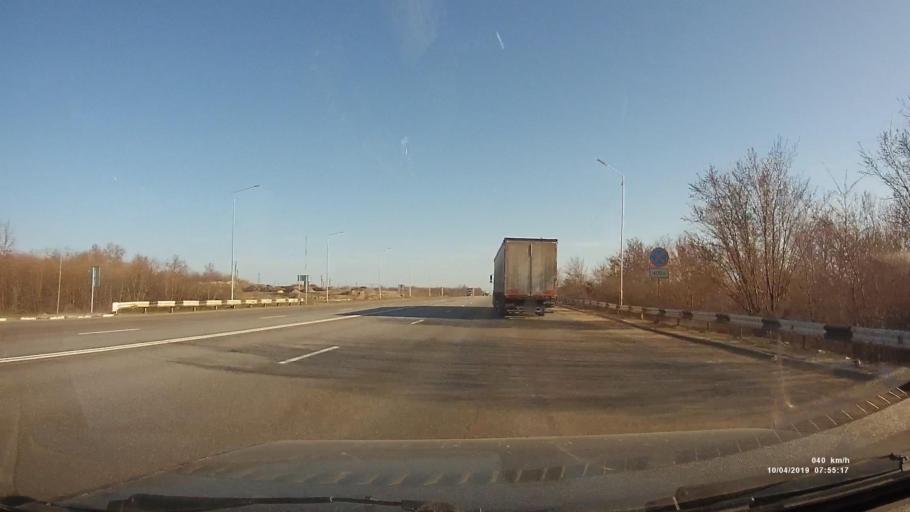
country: RU
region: Rostov
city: Kamensk-Shakhtinskiy
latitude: 48.2770
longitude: 40.2945
